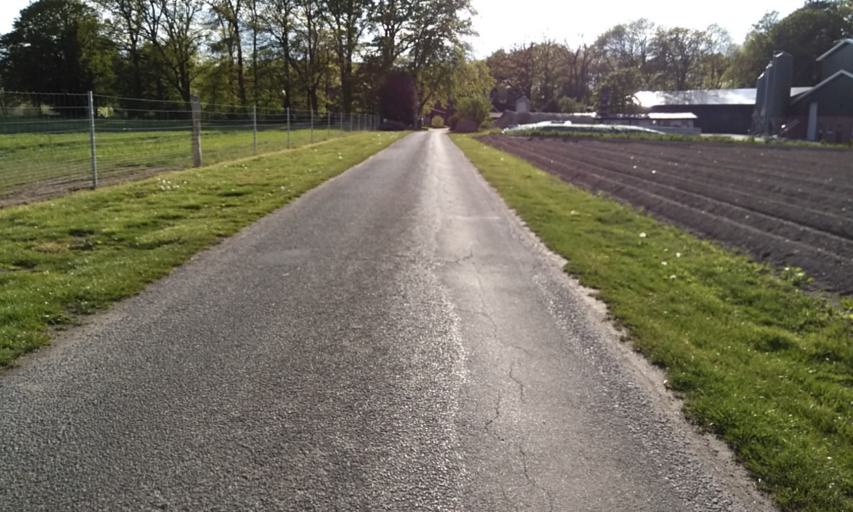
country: DE
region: Lower Saxony
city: Beckdorf
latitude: 53.4077
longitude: 9.6082
